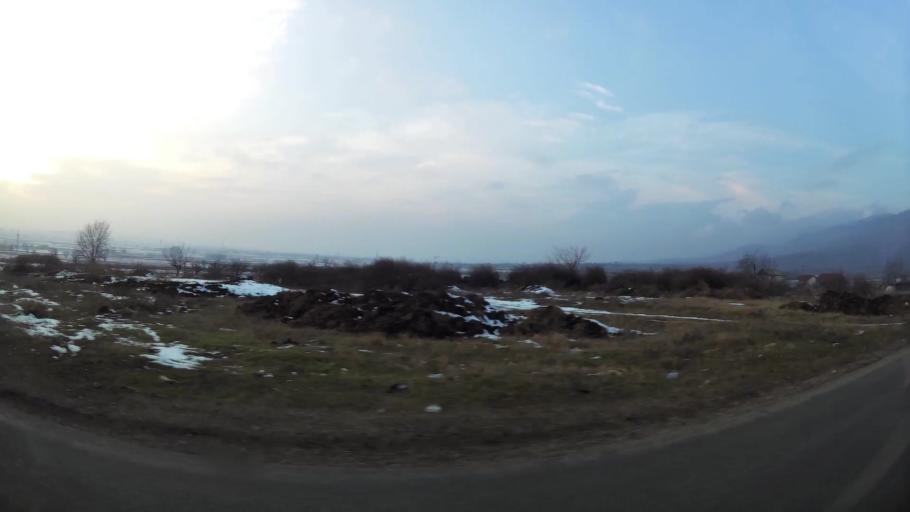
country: MK
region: Aracinovo
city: Arachinovo
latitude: 42.0291
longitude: 21.5456
